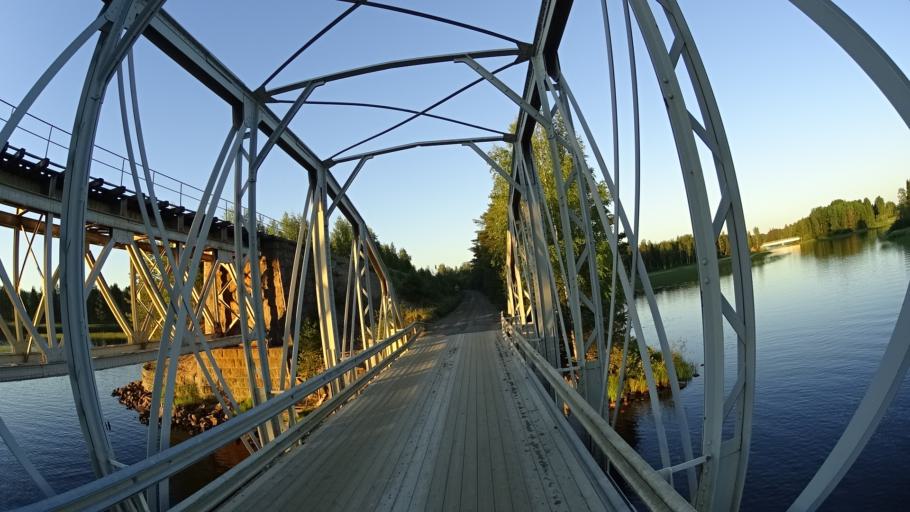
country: FI
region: Central Finland
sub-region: Jyvaeskylae
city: Petaejaevesi
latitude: 62.2555
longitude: 25.1727
